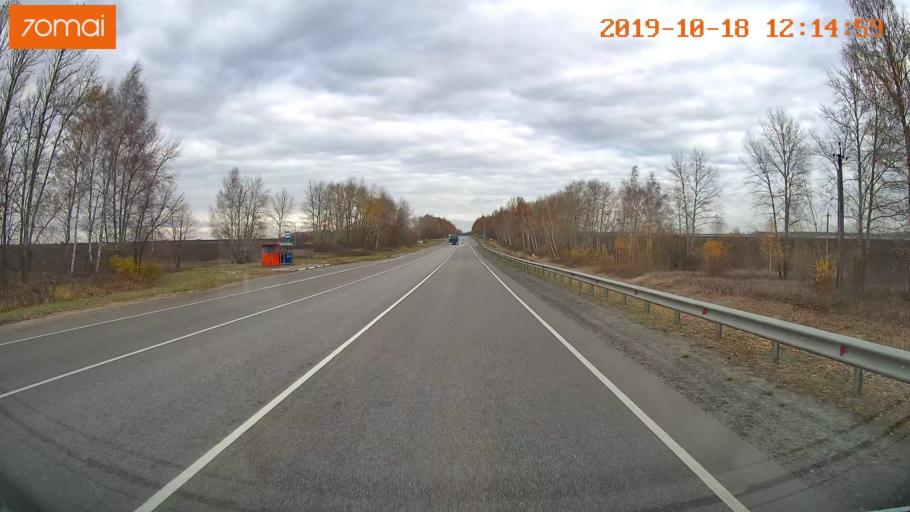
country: RU
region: Rjazan
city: Zakharovo
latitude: 54.4377
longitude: 39.3925
